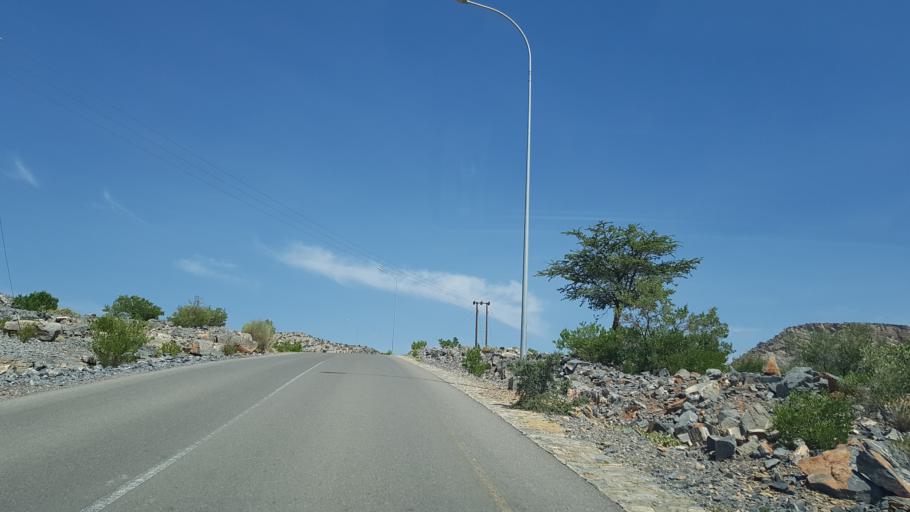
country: OM
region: Al Batinah
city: Bayt al `Awabi
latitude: 23.1369
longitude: 57.5491
